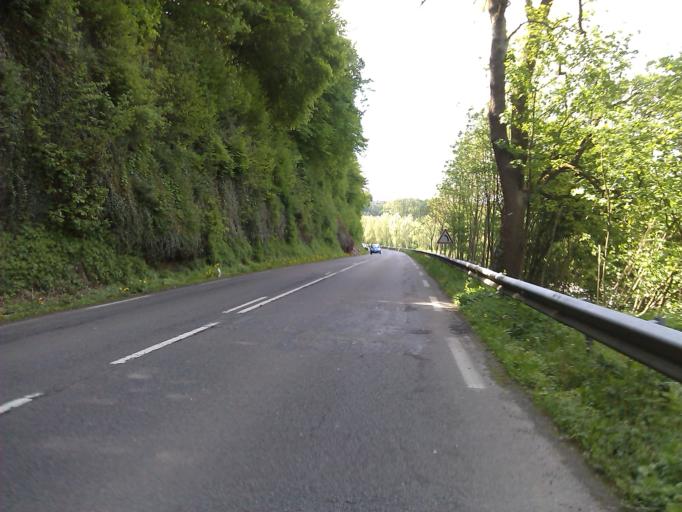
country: FR
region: Franche-Comte
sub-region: Departement du Doubs
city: Courcelles-les-Montbeliard
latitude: 47.5046
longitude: 6.7834
